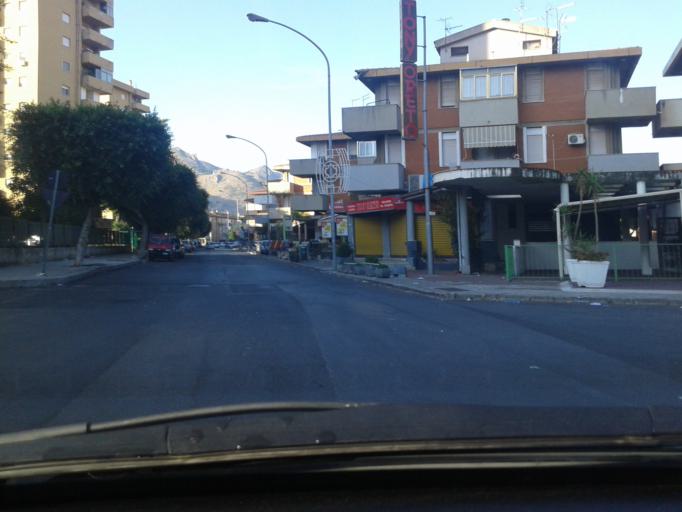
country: IT
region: Sicily
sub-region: Palermo
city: Palermo
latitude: 38.0926
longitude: 13.3607
